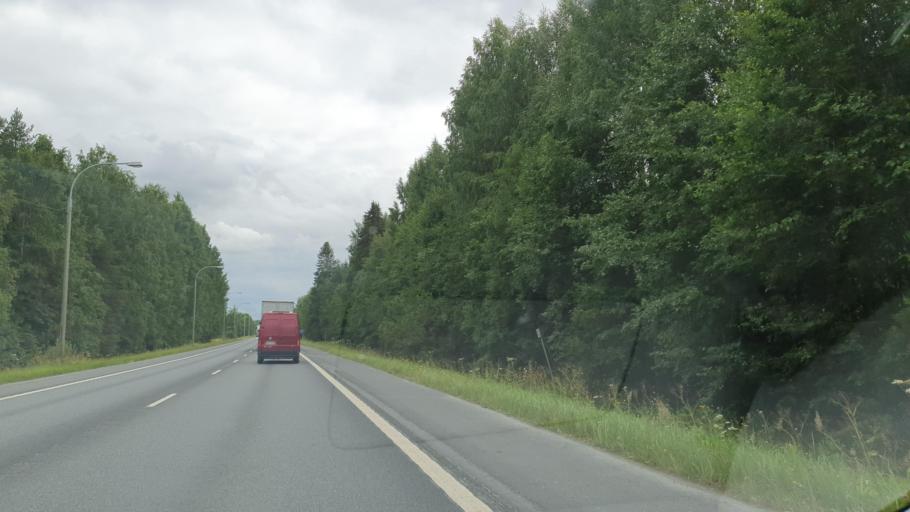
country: FI
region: Northern Savo
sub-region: Ylae-Savo
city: Iisalmi
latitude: 63.5051
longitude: 27.2595
